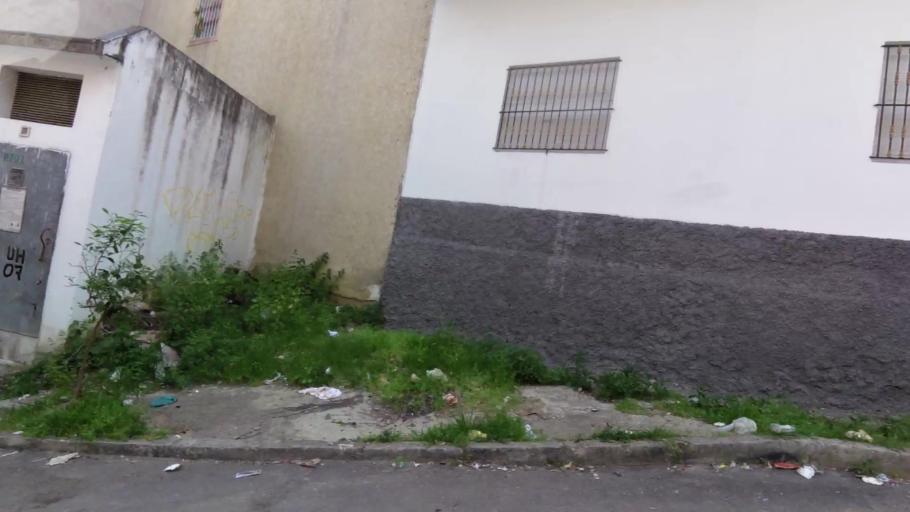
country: MA
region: Tanger-Tetouan
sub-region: Tanger-Assilah
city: Tangier
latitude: 35.7391
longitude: -5.8325
